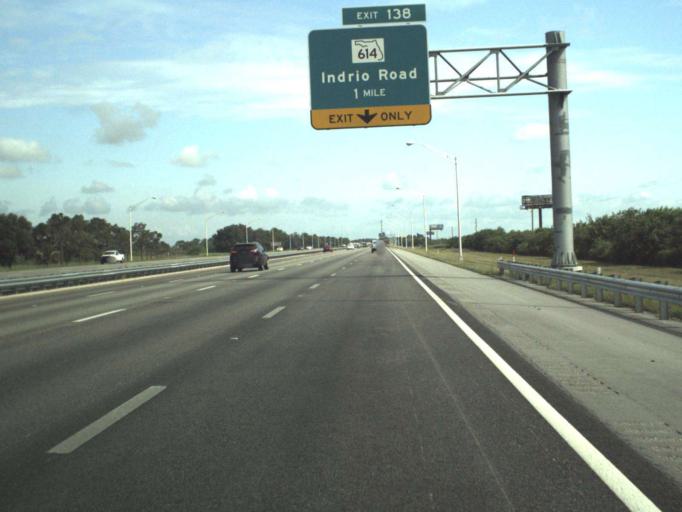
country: US
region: Florida
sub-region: Saint Lucie County
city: Lakewood Park
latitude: 27.5033
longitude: -80.4426
